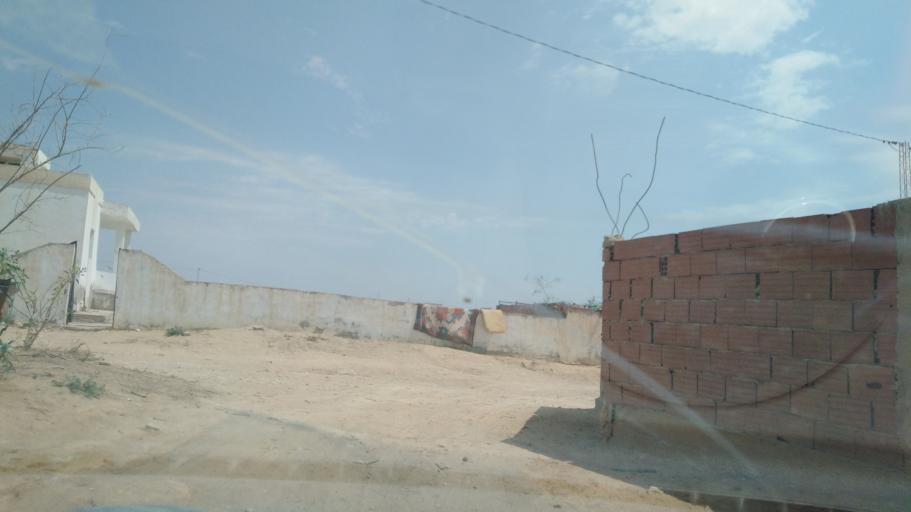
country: TN
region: Safaqis
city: Sfax
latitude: 34.7410
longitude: 10.5616
